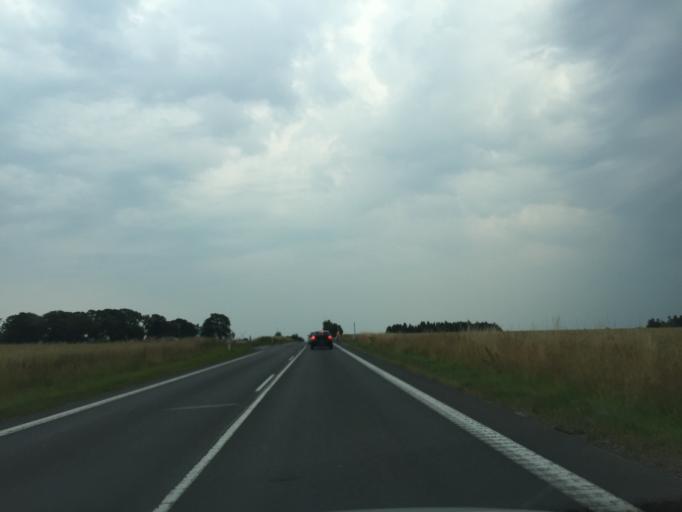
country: DK
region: Central Jutland
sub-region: Viborg Kommune
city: Bjerringbro
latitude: 56.3547
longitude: 9.6758
